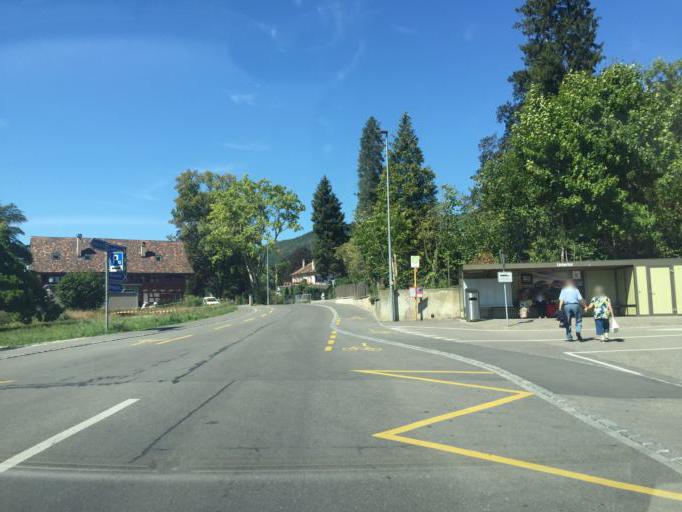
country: CH
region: Schaffhausen
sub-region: Bezirk Stein
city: Stein am Rhein
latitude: 47.6613
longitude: 8.8575
